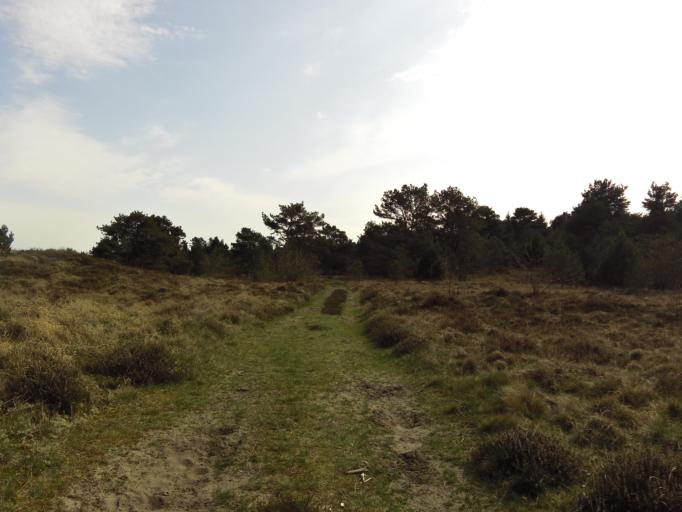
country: DK
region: South Denmark
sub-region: Esbjerg Kommune
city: Ribe
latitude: 55.3199
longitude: 8.8643
